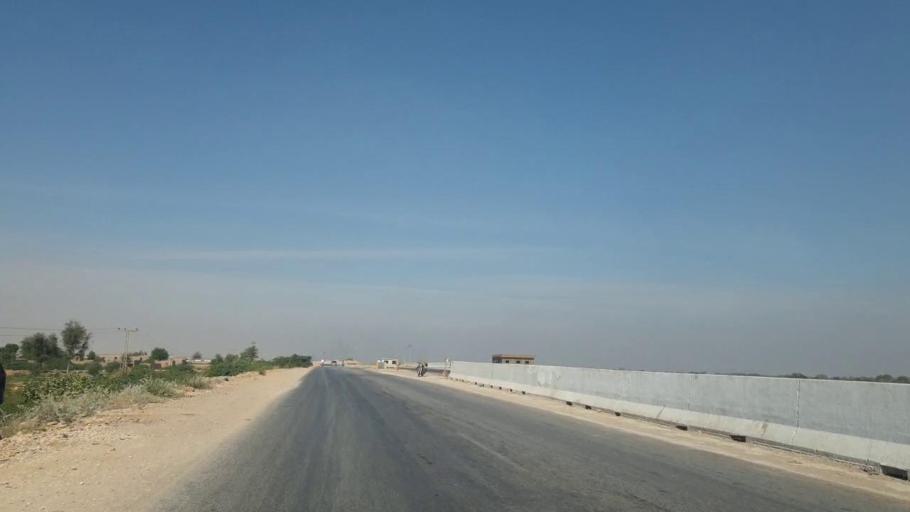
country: PK
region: Sindh
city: Matiari
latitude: 25.6520
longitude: 68.3008
